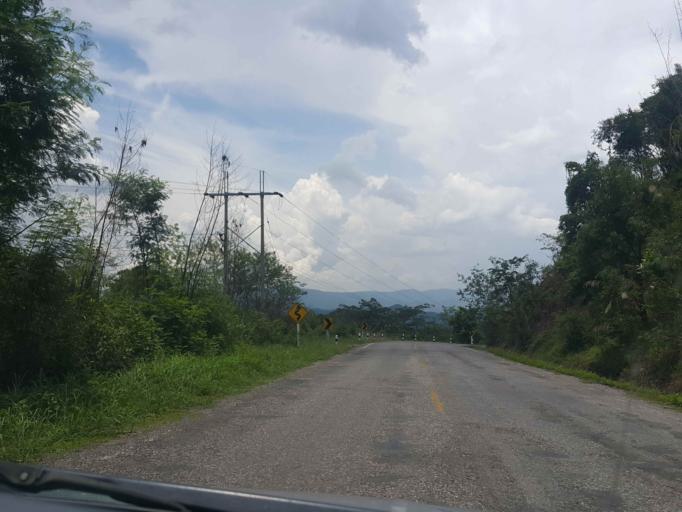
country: TH
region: Phayao
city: Chiang Muan
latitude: 18.9218
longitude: 100.2024
